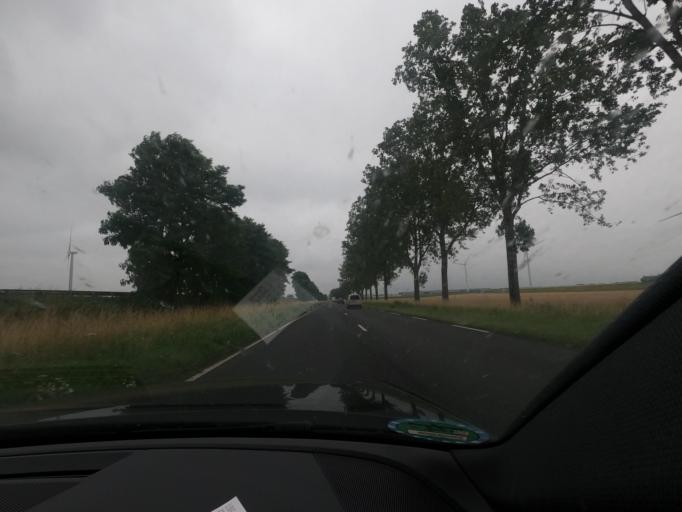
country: FR
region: Picardie
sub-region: Departement de la Somme
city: Roye
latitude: 49.7170
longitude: 2.7448
